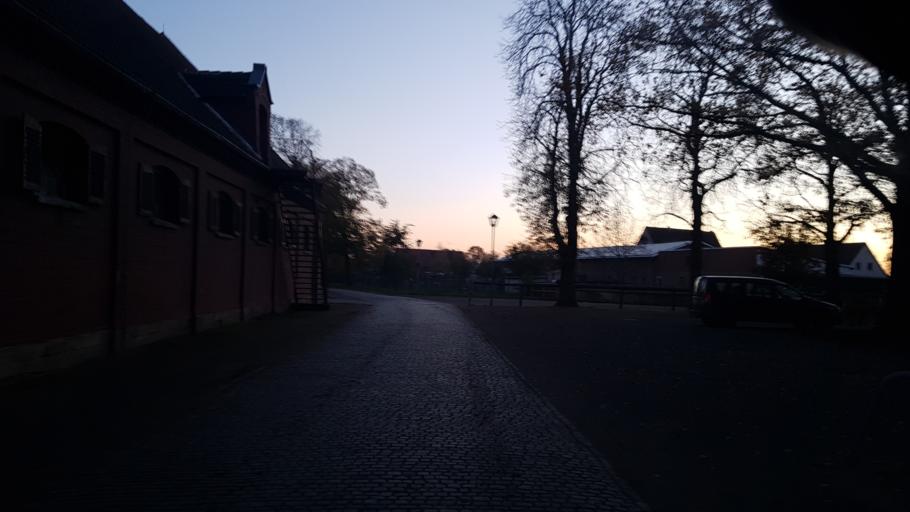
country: DE
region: Saxony
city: Beilrode
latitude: 51.5450
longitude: 13.0604
